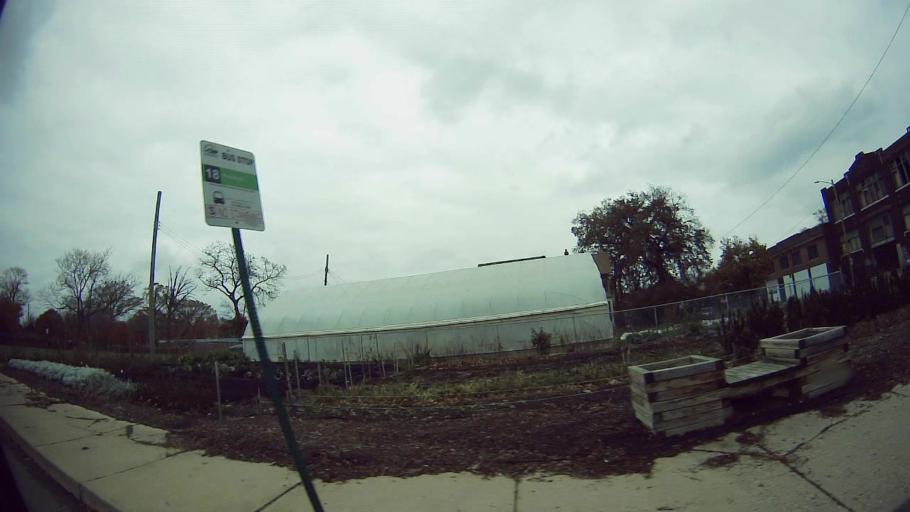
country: US
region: Michigan
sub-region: Wayne County
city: Detroit
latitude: 42.3486
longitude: -83.0817
